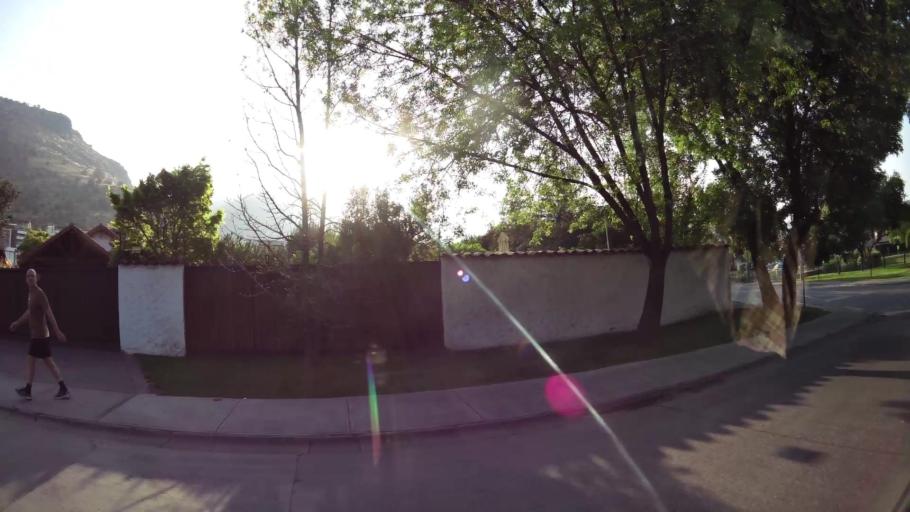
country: CL
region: Santiago Metropolitan
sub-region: Provincia de Santiago
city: Villa Presidente Frei, Nunoa, Santiago, Chile
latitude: -33.3477
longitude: -70.5468
